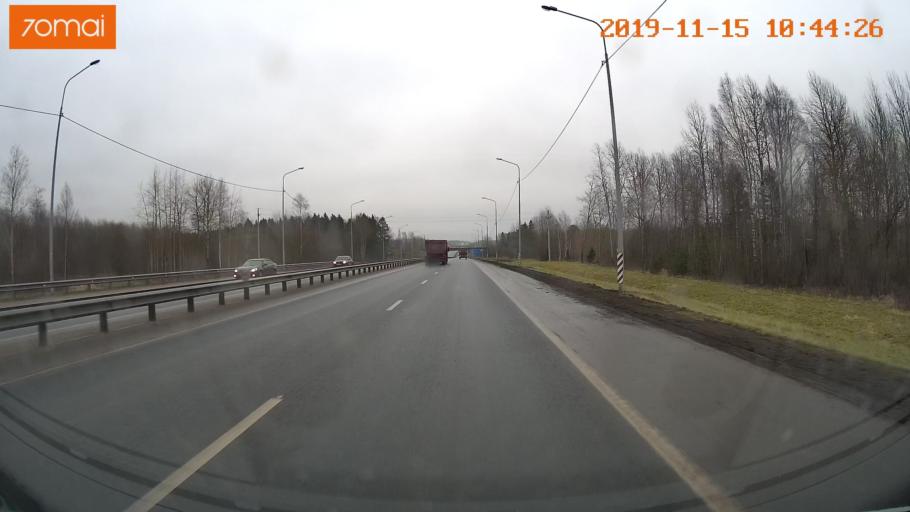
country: RU
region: Vologda
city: Sheksna
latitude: 59.2115
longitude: 38.5576
